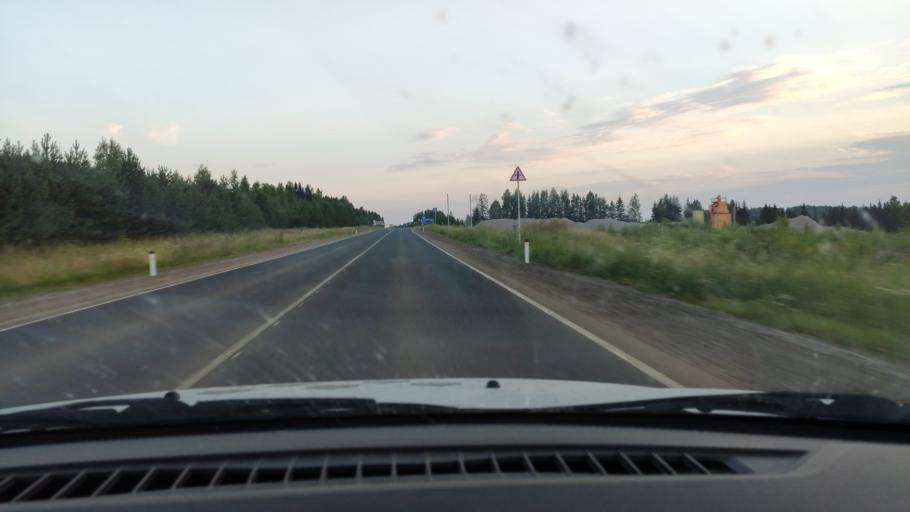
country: RU
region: Perm
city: Siva
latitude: 58.4248
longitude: 54.4540
